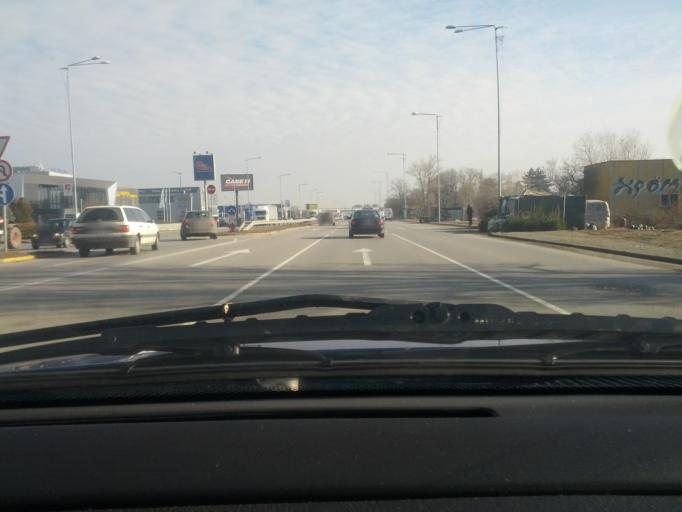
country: BG
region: Sofia-Capital
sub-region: Stolichna Obshtina
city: Sofia
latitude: 42.7090
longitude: 23.4306
